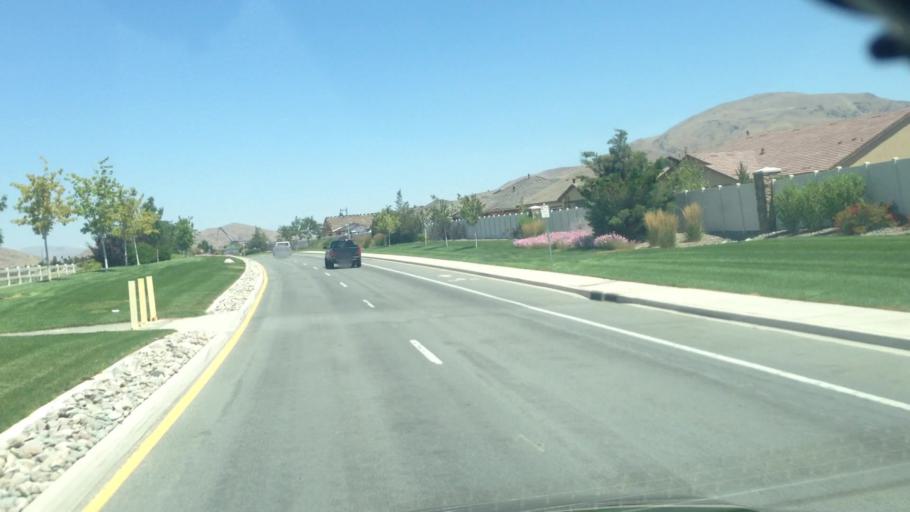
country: US
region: Nevada
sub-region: Washoe County
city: Sparks
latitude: 39.4316
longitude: -119.7289
